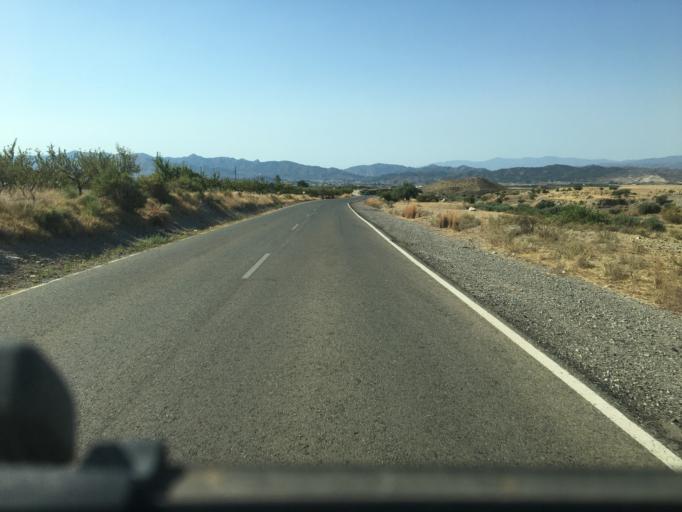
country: ES
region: Andalusia
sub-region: Provincia de Almeria
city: Huercal-Overa
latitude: 37.4375
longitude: -1.9757
